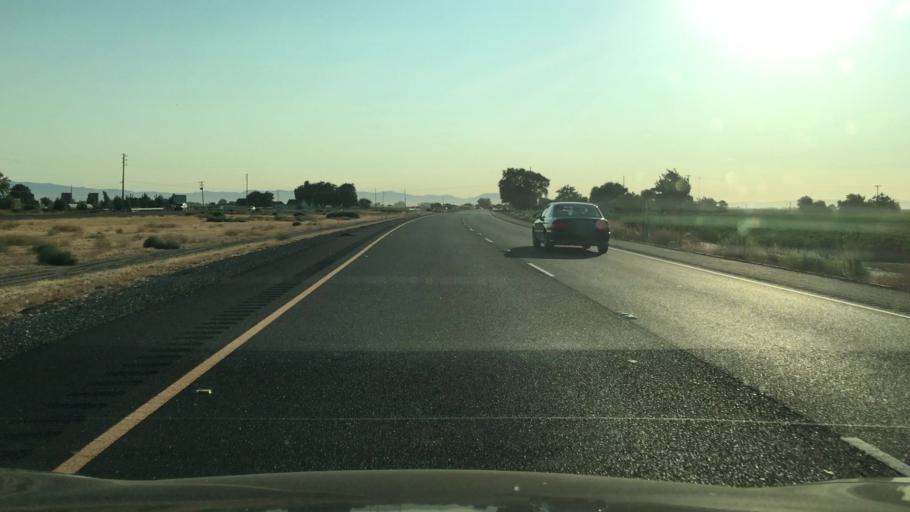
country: US
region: California
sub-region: Merced County
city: Dos Palos
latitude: 37.0488
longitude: -120.5912
